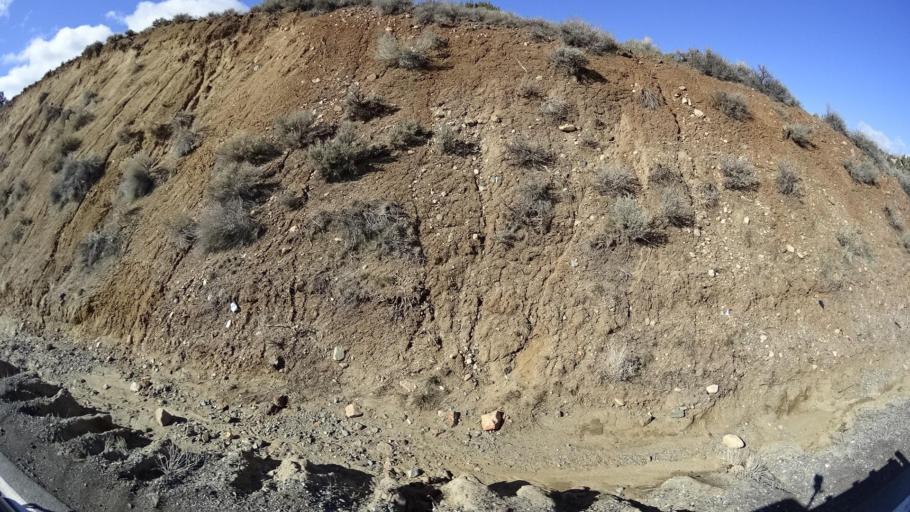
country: US
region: Nevada
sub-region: Washoe County
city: Lemmon Valley
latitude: 39.7337
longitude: -119.8814
